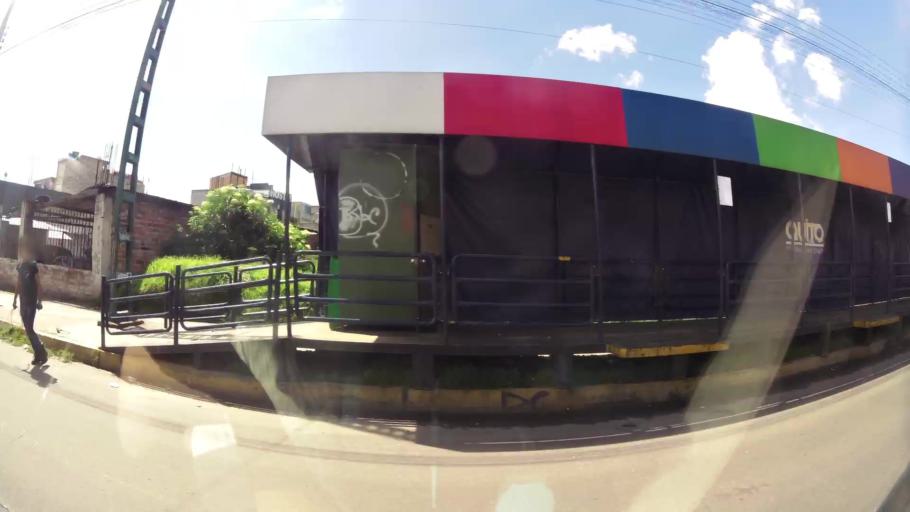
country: EC
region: Pichincha
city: Quito
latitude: -0.2905
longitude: -78.5455
